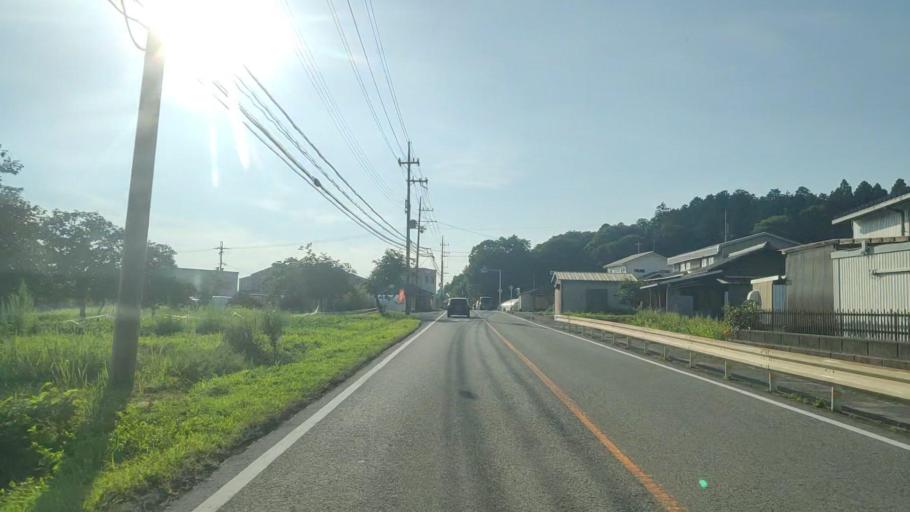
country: JP
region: Shiga Prefecture
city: Hikone
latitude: 35.2377
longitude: 136.2905
